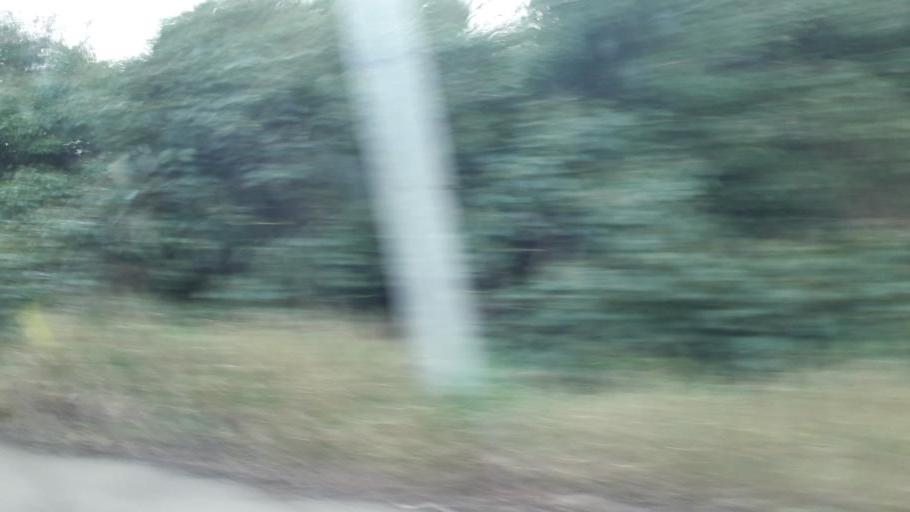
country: IE
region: Leinster
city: An Ros
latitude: 53.5195
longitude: -6.1347
